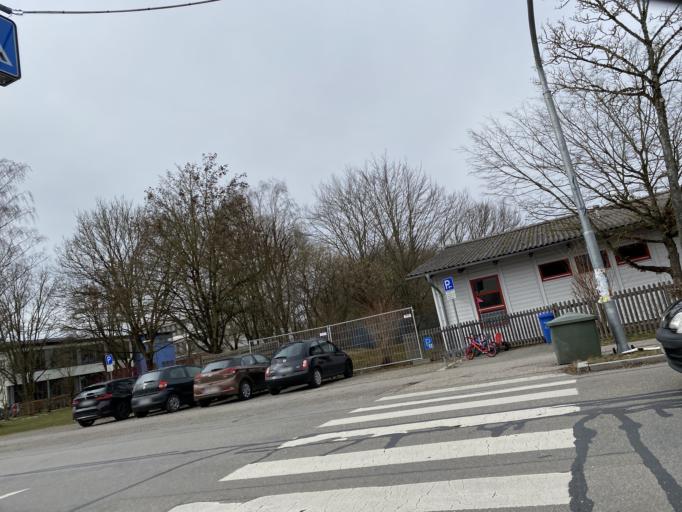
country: DE
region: Bavaria
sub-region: Upper Bavaria
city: Fuerstenfeldbruck
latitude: 48.1678
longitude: 11.2263
